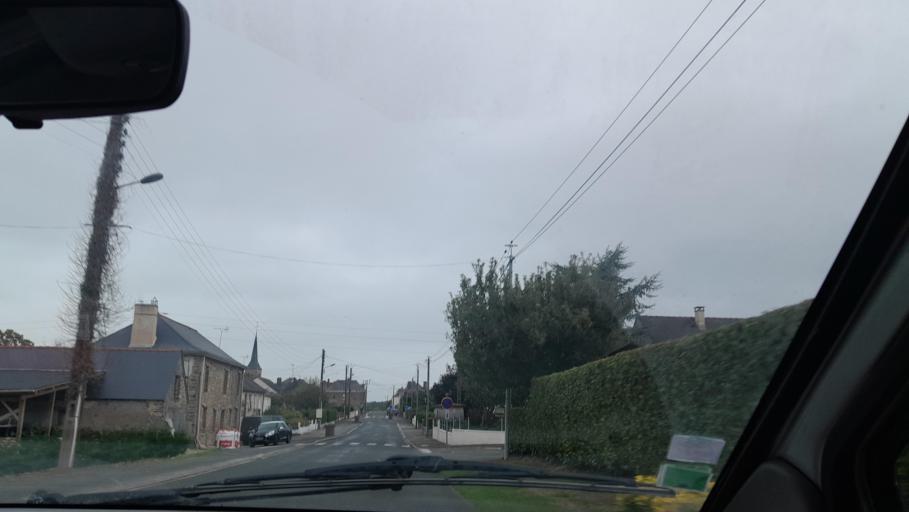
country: FR
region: Pays de la Loire
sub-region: Departement de Maine-et-Loire
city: Pouance
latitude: 47.7146
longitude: -1.1781
